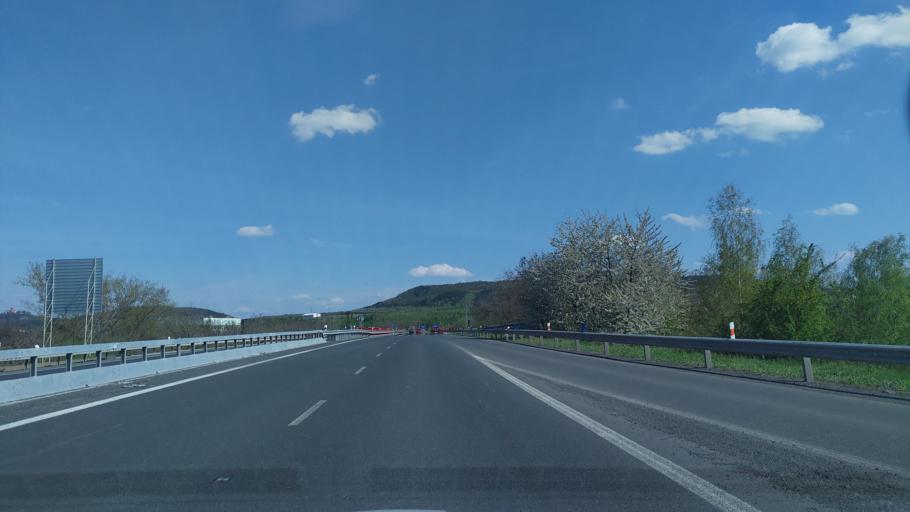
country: CZ
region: Ustecky
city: Horni Jiretin
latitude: 50.5258
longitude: 13.5798
